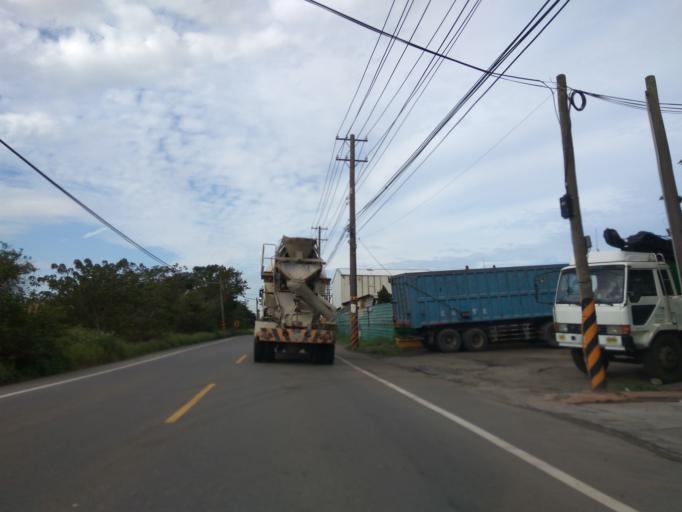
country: TW
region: Taiwan
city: Daxi
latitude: 24.9416
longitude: 121.1567
